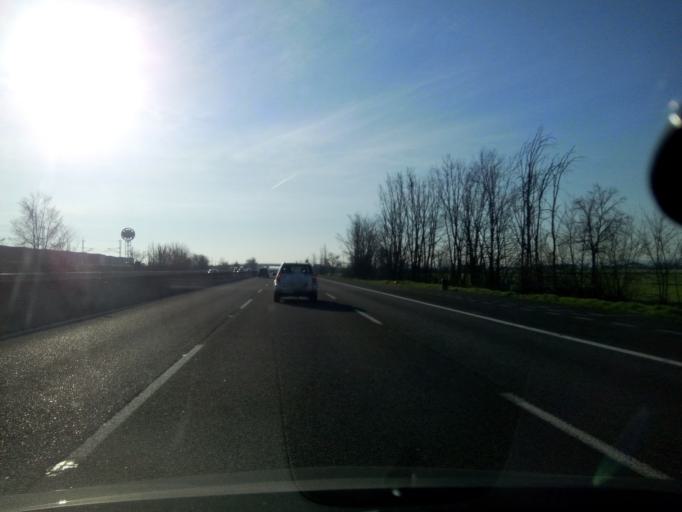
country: IT
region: Emilia-Romagna
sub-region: Provincia di Reggio Emilia
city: Caprara
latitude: 44.7733
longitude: 10.5085
